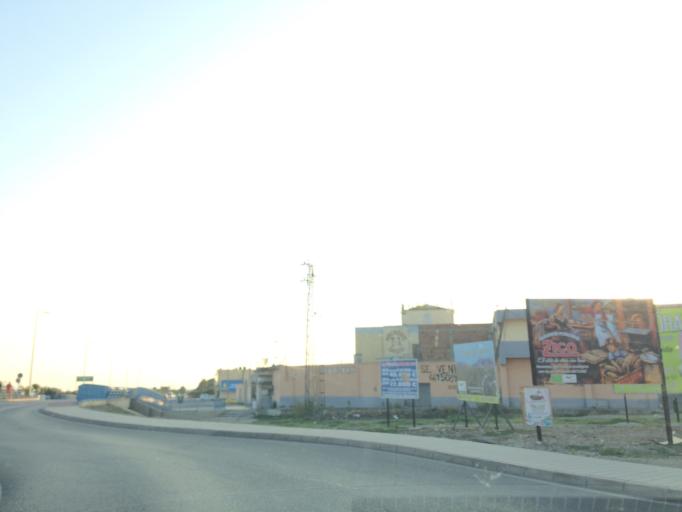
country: ES
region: Andalusia
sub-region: Provincia de Almeria
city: Nijar
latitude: 36.9334
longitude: -2.1363
